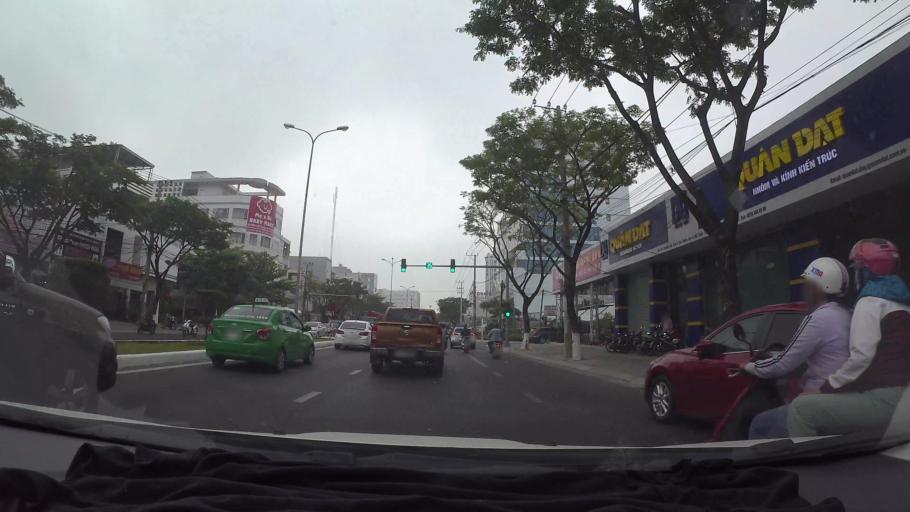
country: VN
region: Da Nang
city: Cam Le
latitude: 16.0424
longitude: 108.2102
